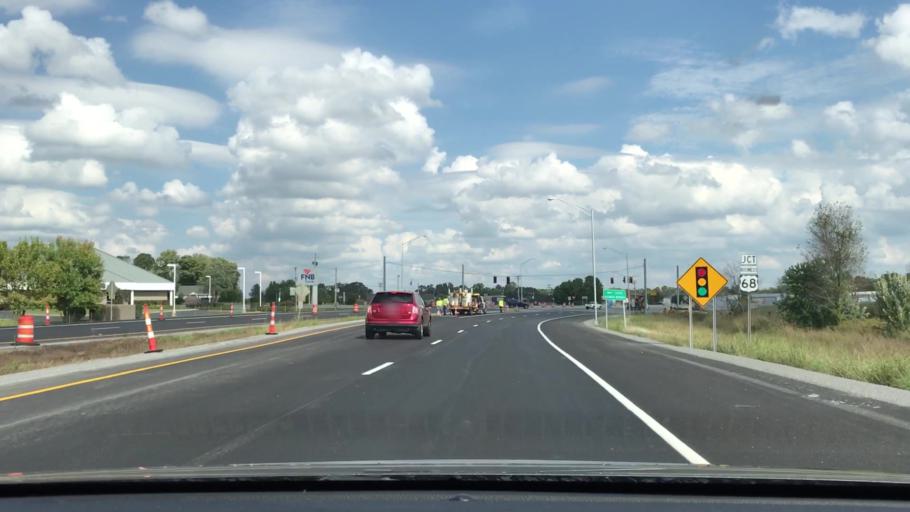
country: US
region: Kentucky
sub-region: Trigg County
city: Cadiz
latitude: 36.8648
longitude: -87.7969
